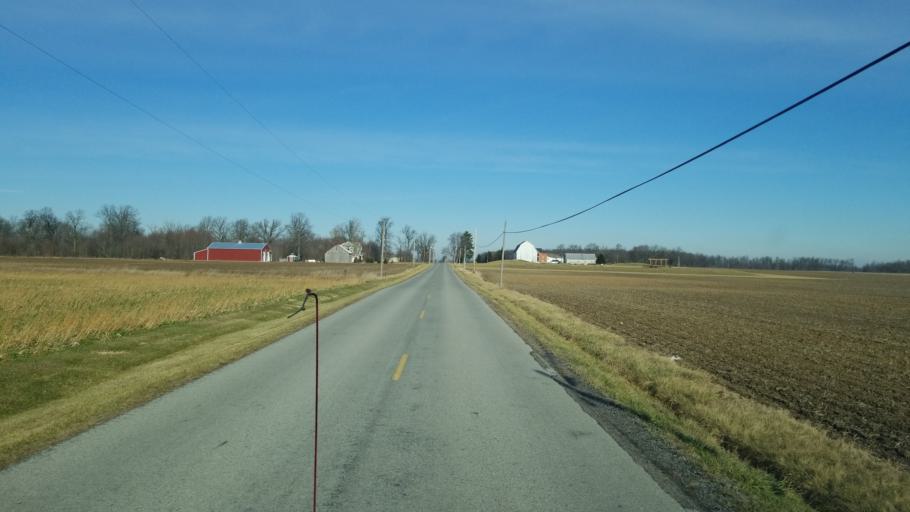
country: US
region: Ohio
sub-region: Allen County
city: Bluffton
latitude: 40.8423
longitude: -83.8993
